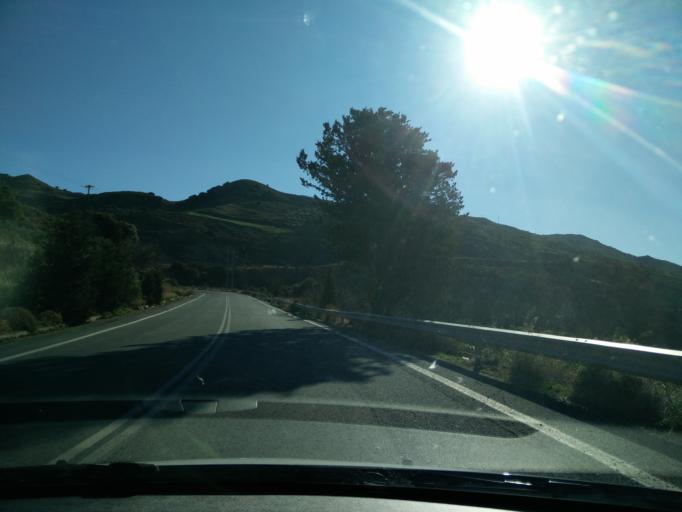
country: GR
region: Crete
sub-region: Nomos Irakleiou
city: Arkalochori
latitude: 35.0725
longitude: 25.3596
